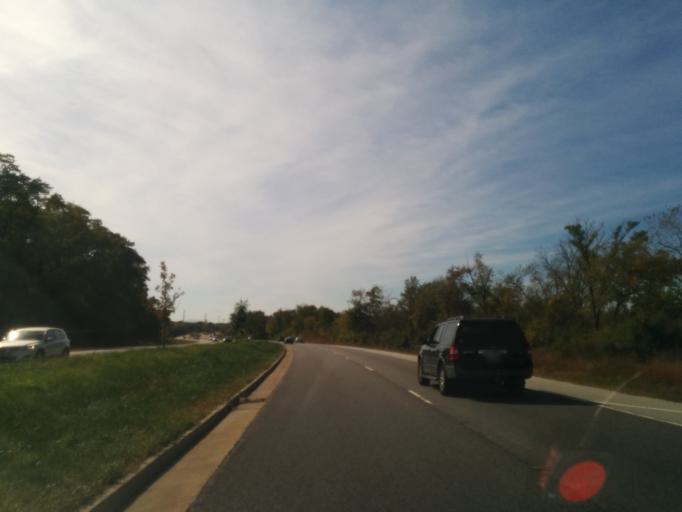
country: US
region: Illinois
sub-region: DuPage County
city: Warrenville
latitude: 41.8295
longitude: -88.1718
